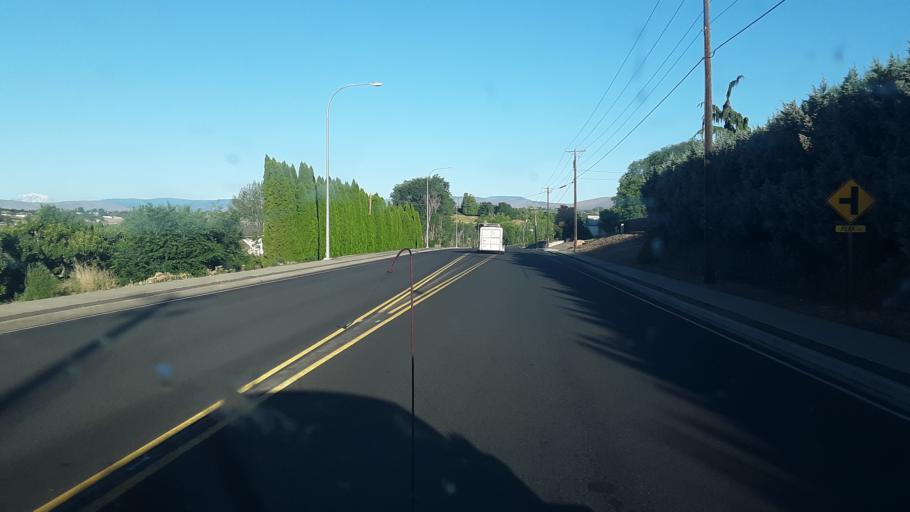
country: US
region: Washington
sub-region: Yakima County
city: West Valley
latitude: 46.6003
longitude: -120.6390
